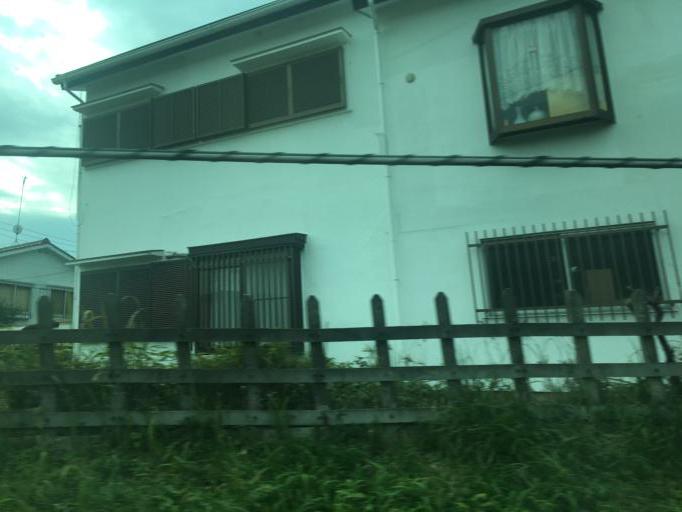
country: JP
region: Tokyo
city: Hino
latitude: 35.6890
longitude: 139.4258
